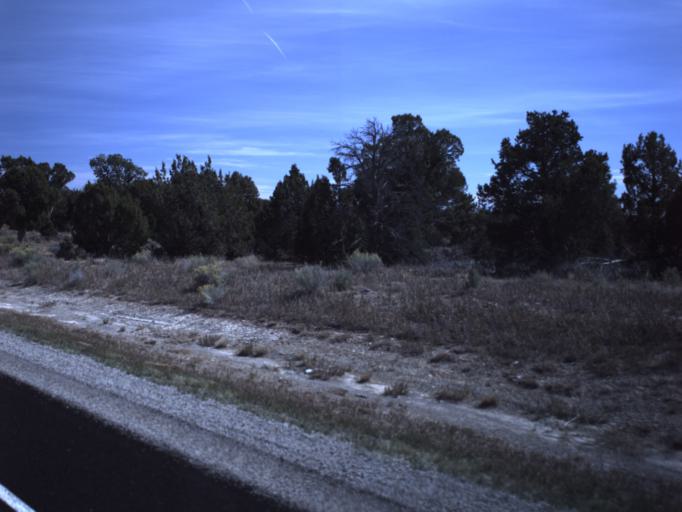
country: US
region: Colorado
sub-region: Dolores County
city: Dove Creek
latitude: 37.8230
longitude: -109.0647
